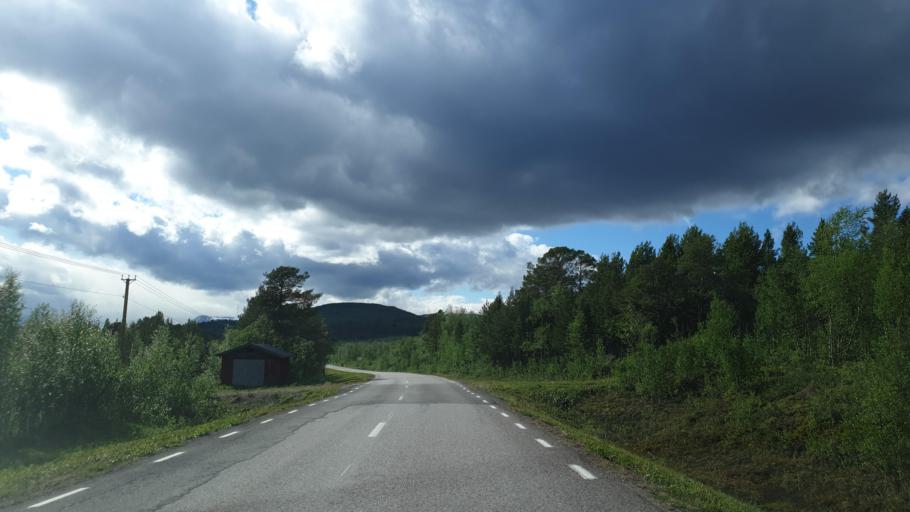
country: SE
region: Norrbotten
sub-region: Kiruna Kommun
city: Kiruna
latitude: 67.8679
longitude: 19.3810
